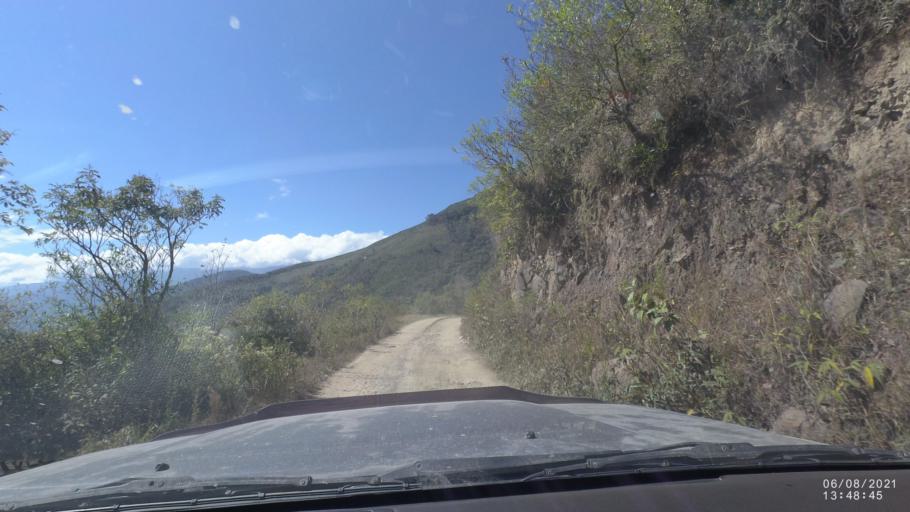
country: BO
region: La Paz
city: Quime
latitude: -16.6627
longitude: -66.7250
